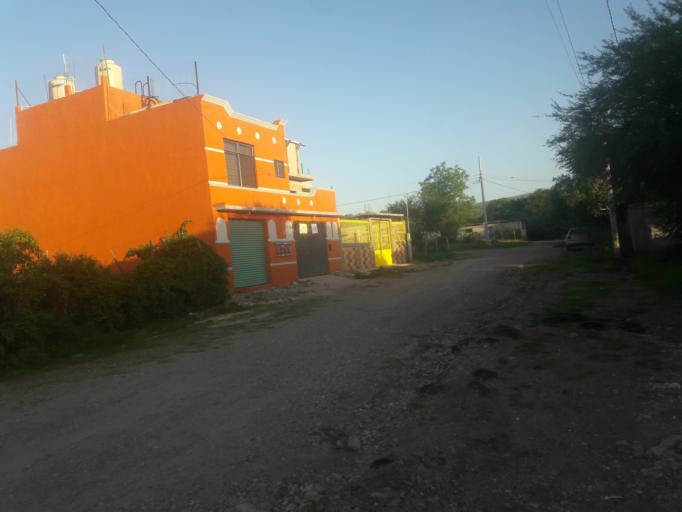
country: MX
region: Oaxaca
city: Ciudad de Huajuapam de Leon
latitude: 17.8063
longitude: -97.7942
